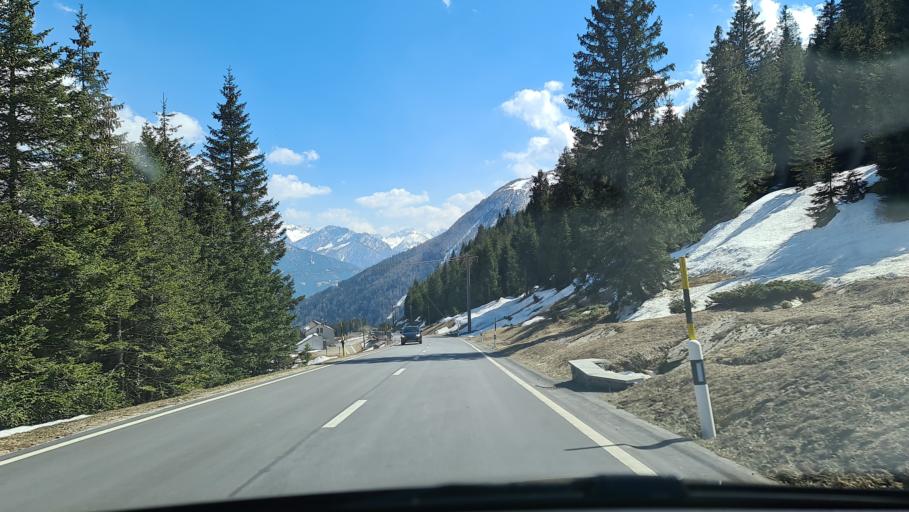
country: CH
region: Grisons
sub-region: Moesa District
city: Mesocco
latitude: 46.4451
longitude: 9.2014
